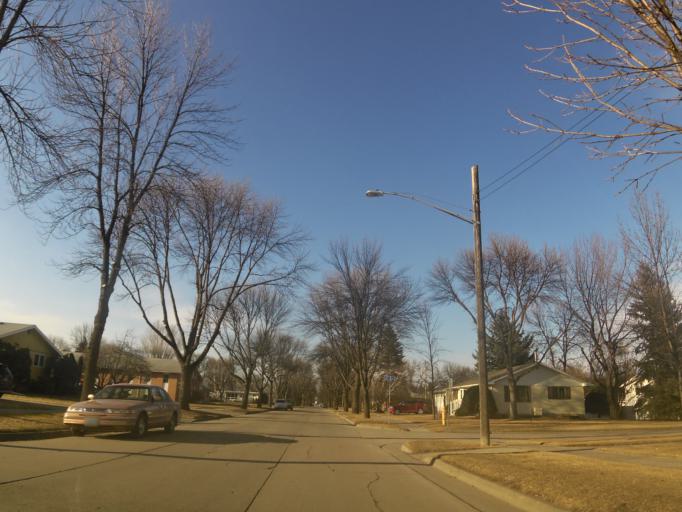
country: US
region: North Dakota
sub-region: Grand Forks County
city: Grand Forks
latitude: 47.9099
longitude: -97.0511
